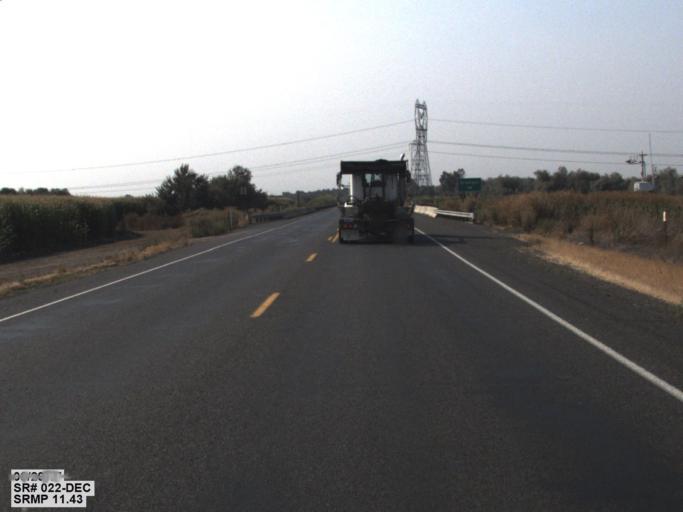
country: US
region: Washington
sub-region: Yakima County
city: Granger
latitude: 46.3032
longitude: -120.1993
